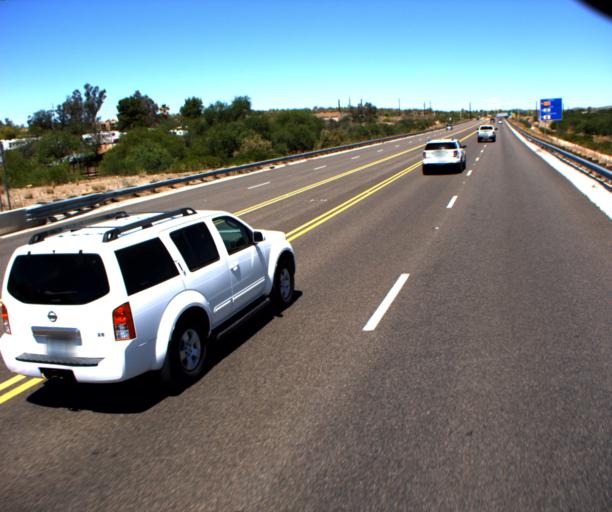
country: US
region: Arizona
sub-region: Maricopa County
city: Wickenburg
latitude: 33.9818
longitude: -112.7353
